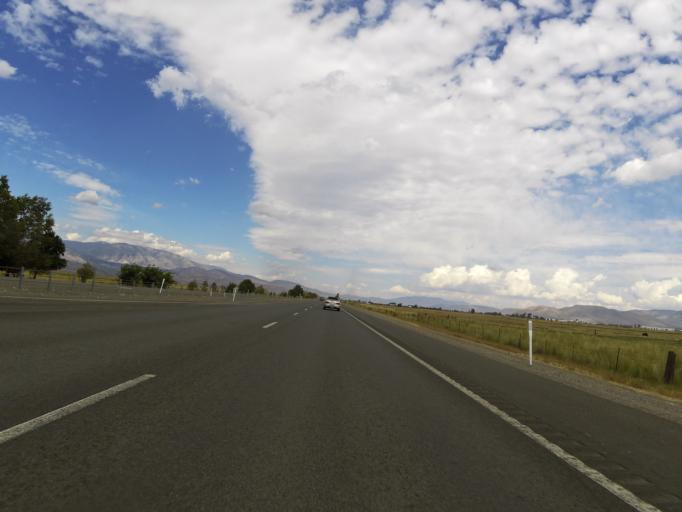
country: US
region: Nevada
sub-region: Douglas County
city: Minden
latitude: 38.9794
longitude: -119.7794
